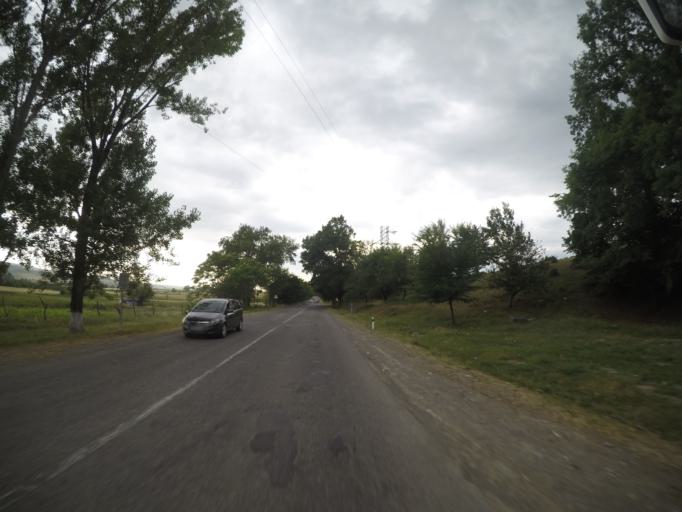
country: AZ
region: Ismayilli
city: Ismayilli
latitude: 40.7703
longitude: 48.2081
